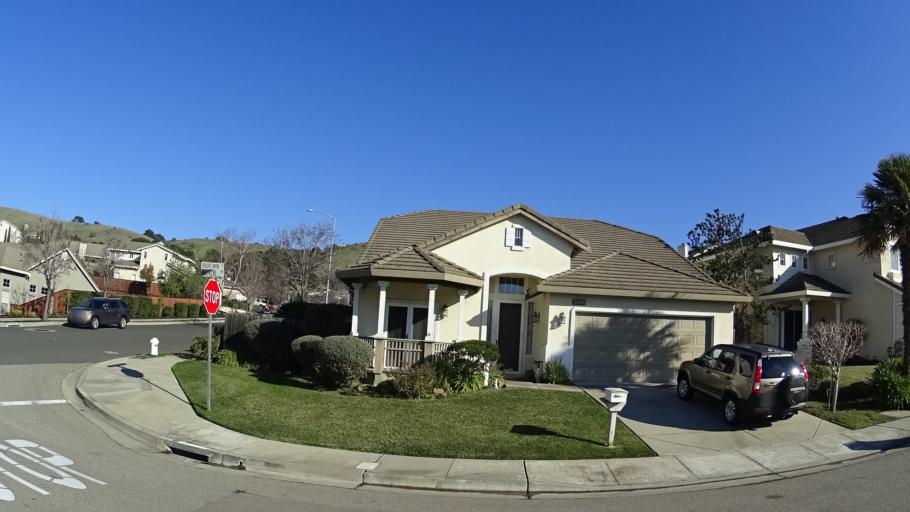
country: US
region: California
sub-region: Alameda County
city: Fairview
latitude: 37.6907
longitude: -122.0362
